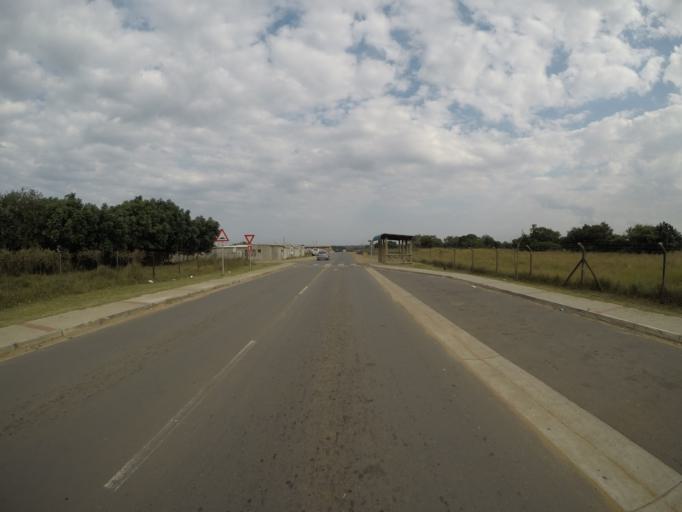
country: ZA
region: KwaZulu-Natal
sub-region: uThungulu District Municipality
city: Richards Bay
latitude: -28.7452
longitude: 32.0903
